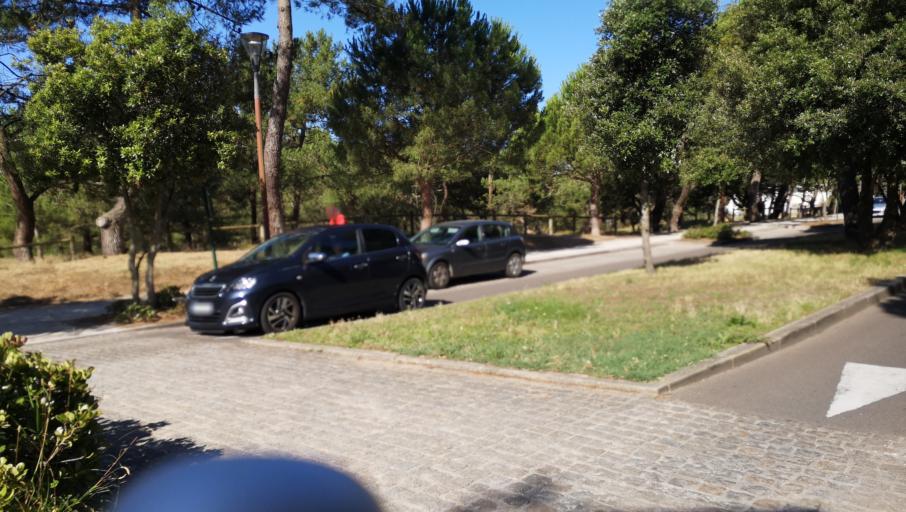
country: FR
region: Pays de la Loire
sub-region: Departement de la Vendee
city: Les Sables-d'Olonne
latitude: 46.4870
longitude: -1.7623
